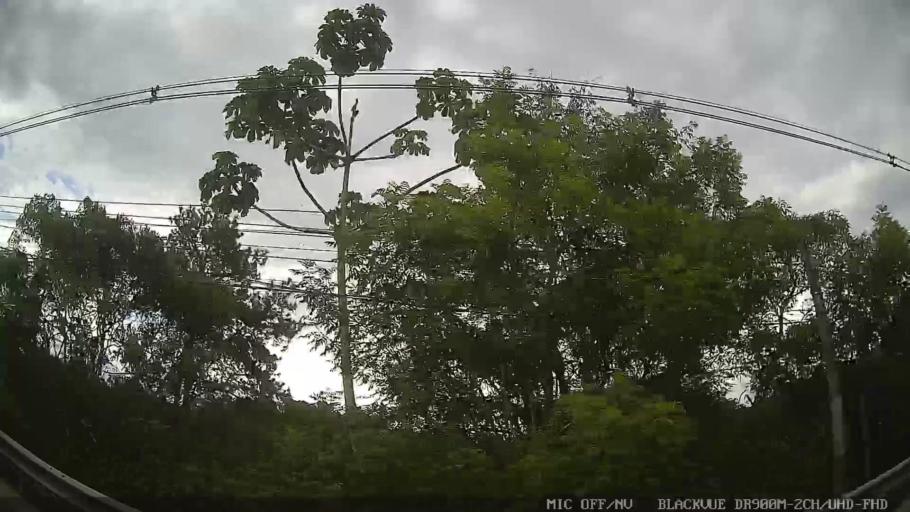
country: BR
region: Sao Paulo
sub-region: Biritiba-Mirim
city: Biritiba Mirim
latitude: -23.5662
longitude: -46.0189
